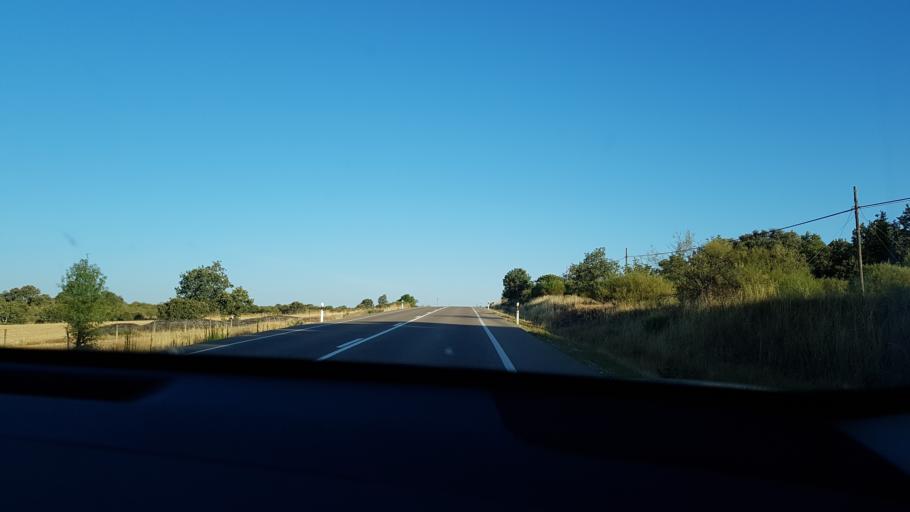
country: ES
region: Castille and Leon
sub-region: Provincia de Zamora
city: Samir de los Canos
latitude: 41.6504
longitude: -6.1717
